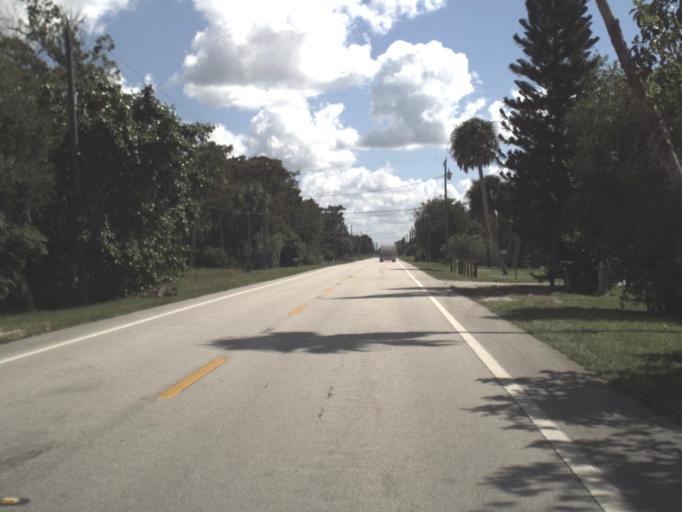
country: US
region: Florida
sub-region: Okeechobee County
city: Taylor Creek
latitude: 27.1717
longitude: -80.7245
